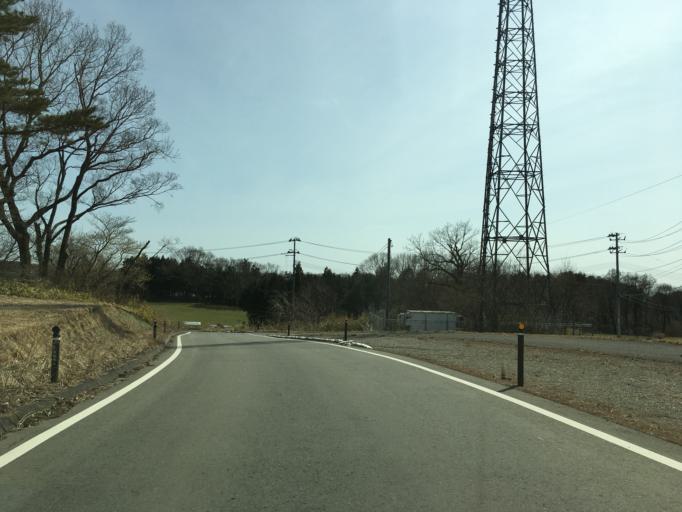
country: JP
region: Fukushima
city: Nihommatsu
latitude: 37.6285
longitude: 140.3602
